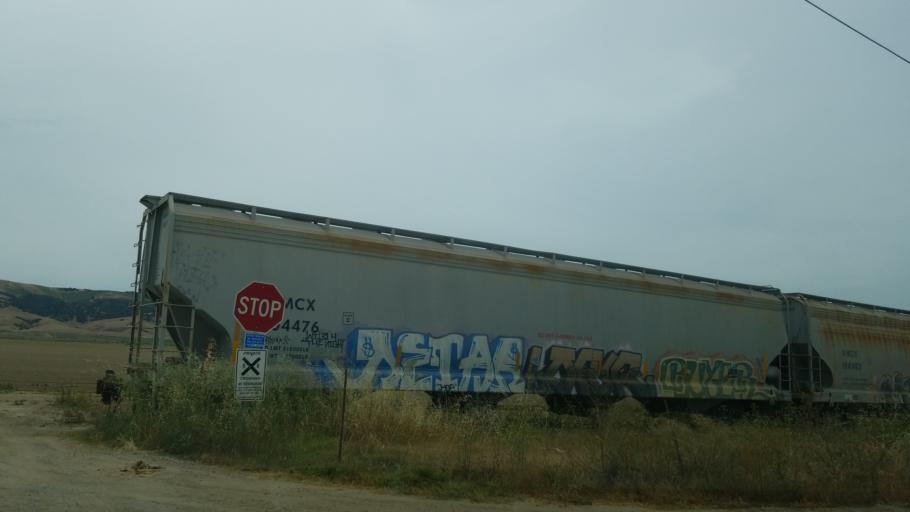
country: US
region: California
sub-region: Santa Barbara County
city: Guadalupe
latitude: 34.9206
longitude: -120.5226
